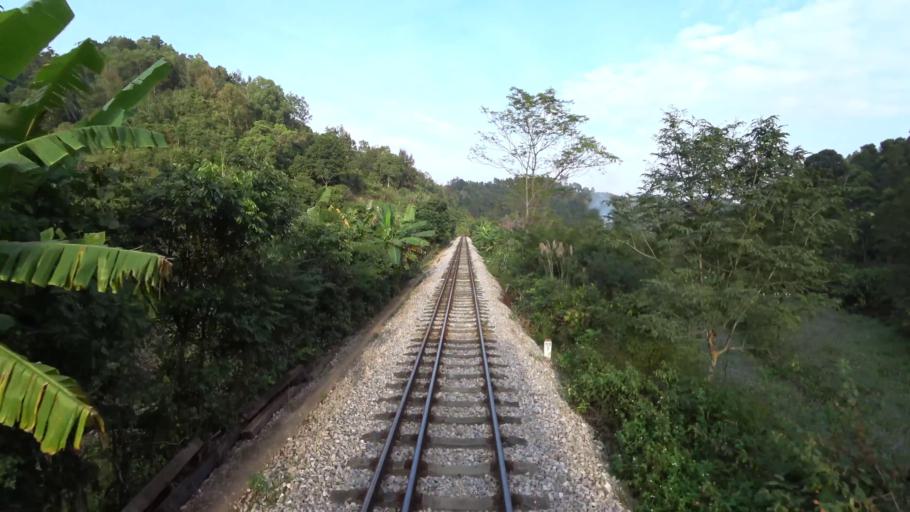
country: VN
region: Lang Son
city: Thi Tran Cao Loc
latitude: 21.9242
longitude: 106.7130
